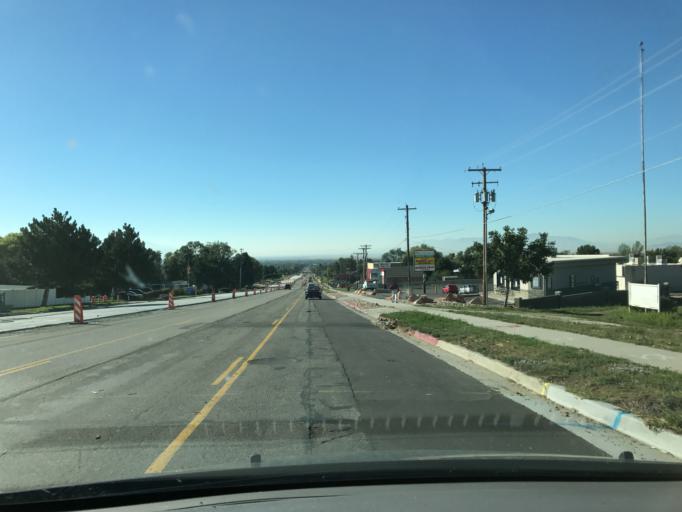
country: US
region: Utah
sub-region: Davis County
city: Hill Air Force Bace
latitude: 41.0991
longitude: -111.9735
